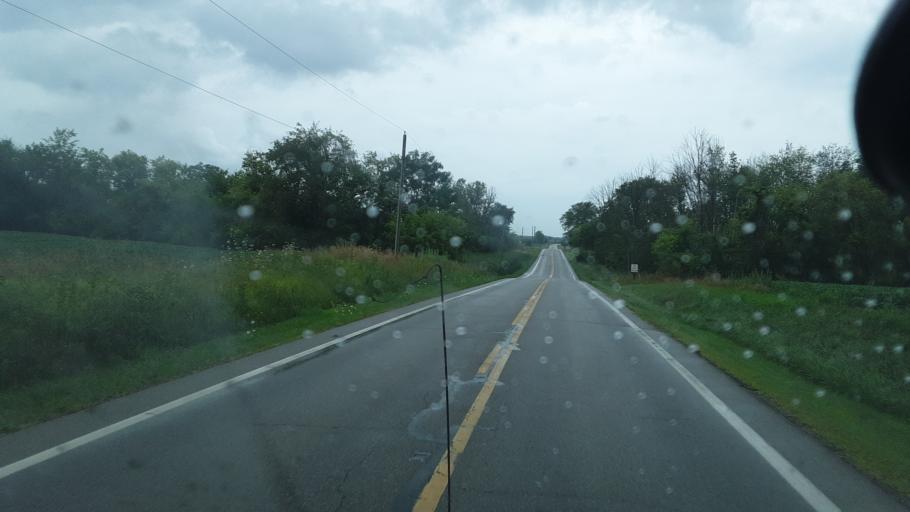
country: US
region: Ohio
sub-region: Williams County
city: Edgerton
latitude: 41.5564
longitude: -84.7920
